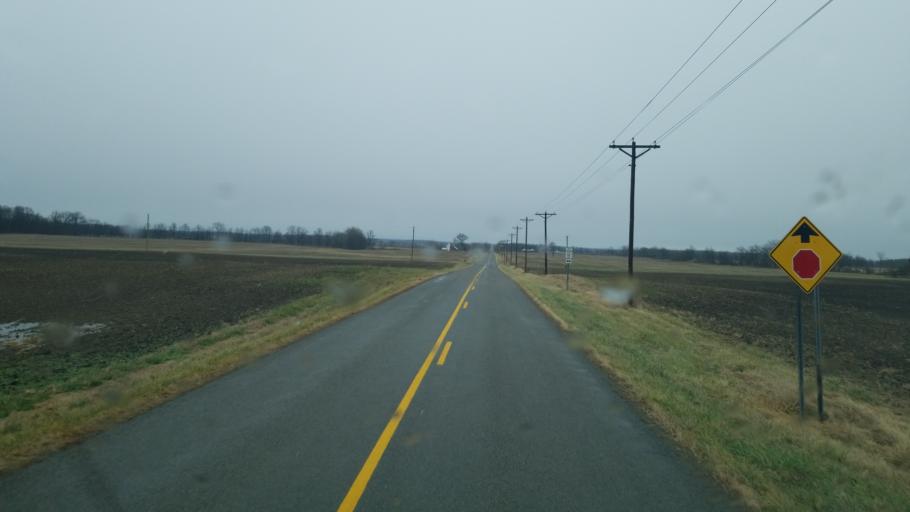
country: US
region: Ohio
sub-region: Logan County
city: Northwood
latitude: 40.4457
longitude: -83.6345
